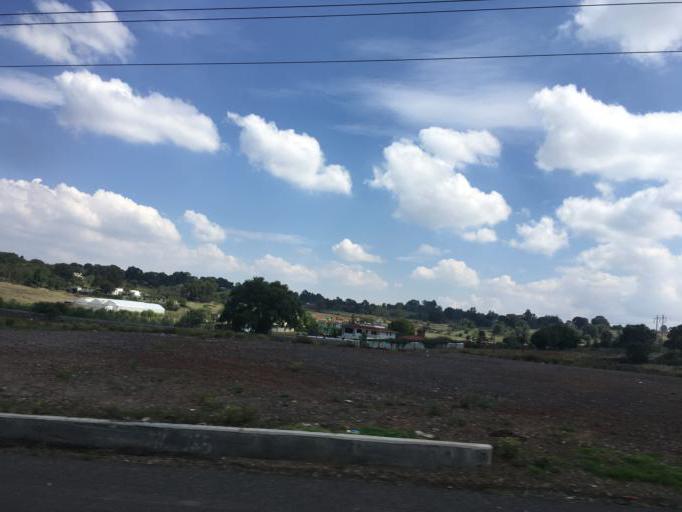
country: MX
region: Mexico
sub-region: Jilotepec
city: Doxhicho
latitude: 19.8897
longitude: -99.6359
